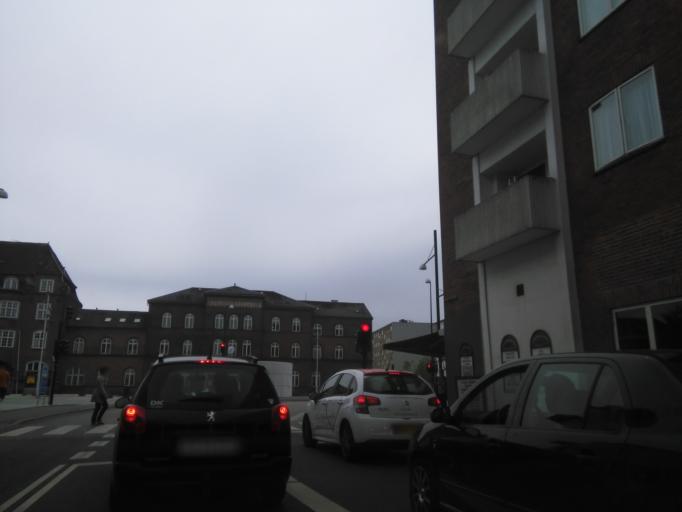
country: DK
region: Central Jutland
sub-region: Horsens Kommune
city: Horsens
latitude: 55.8626
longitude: 9.8428
